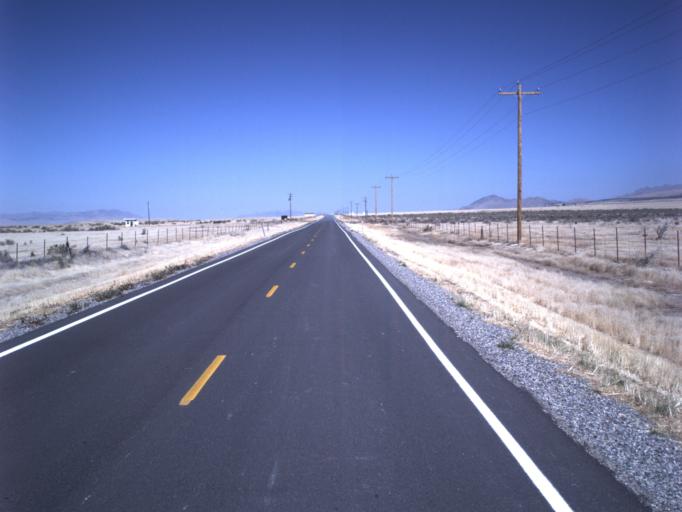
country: US
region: Utah
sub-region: Tooele County
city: Grantsville
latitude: 40.3662
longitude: -112.7461
